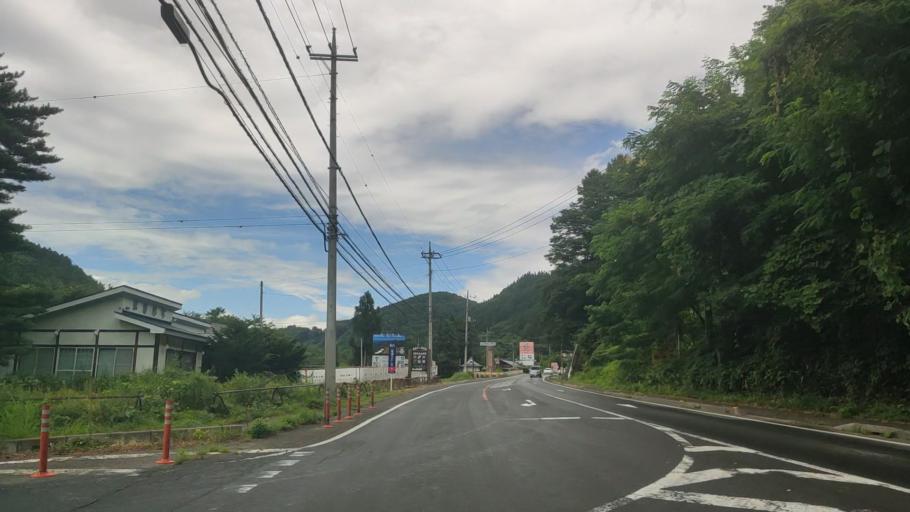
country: JP
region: Gunma
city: Numata
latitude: 36.7409
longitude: 139.2321
